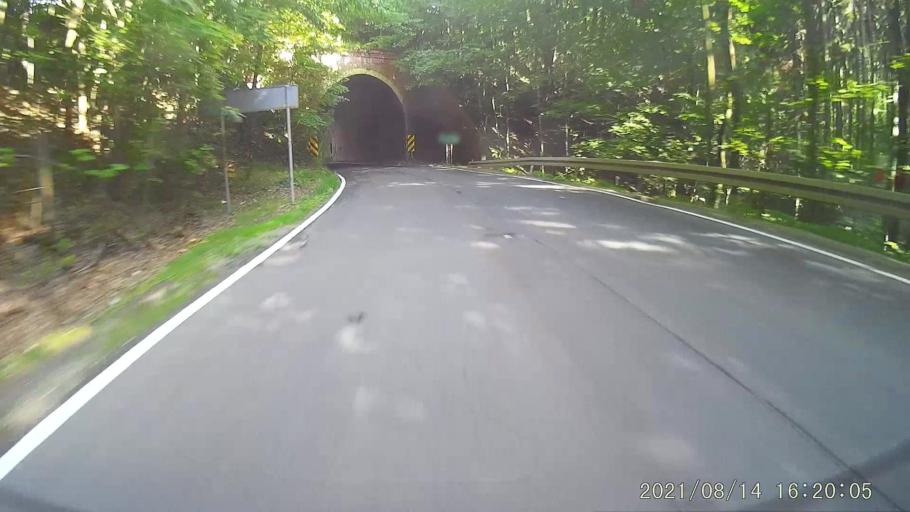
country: PL
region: Lower Silesian Voivodeship
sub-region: Powiat walbrzyski
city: Boguszow-Gorce
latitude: 50.7563
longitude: 16.2303
